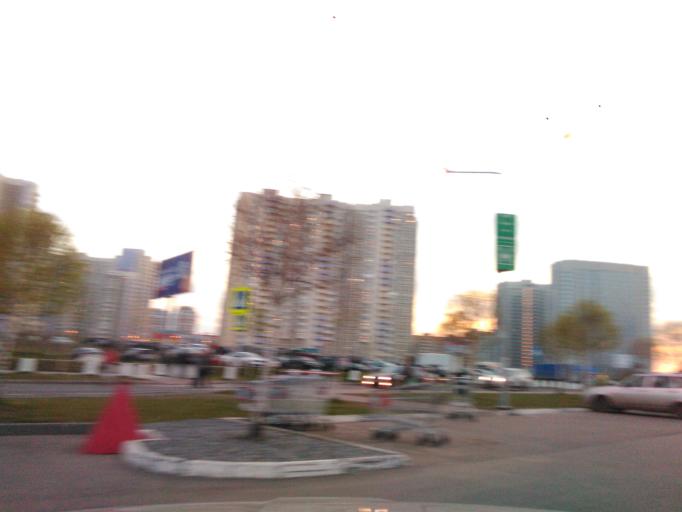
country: RU
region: Moscow
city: Khimki
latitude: 55.9080
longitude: 37.3977
